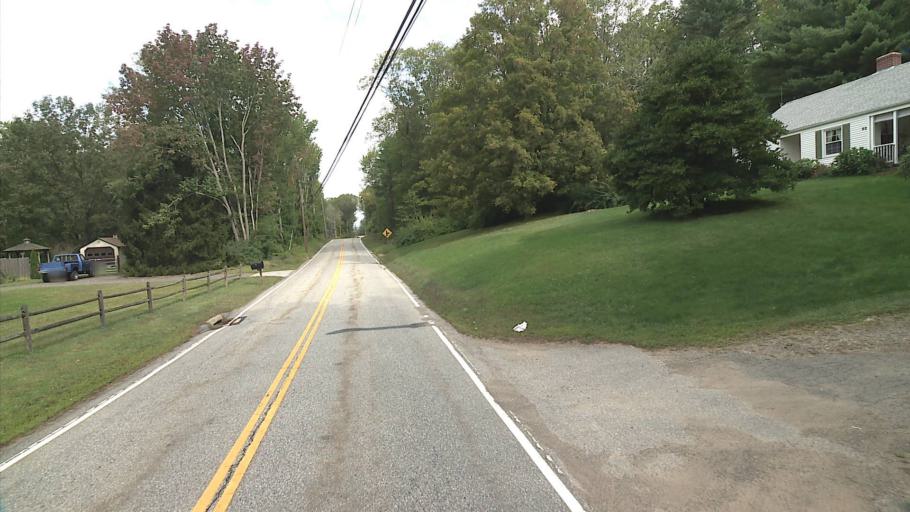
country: US
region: Connecticut
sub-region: Tolland County
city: Stafford Springs
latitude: 41.8886
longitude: -72.2677
